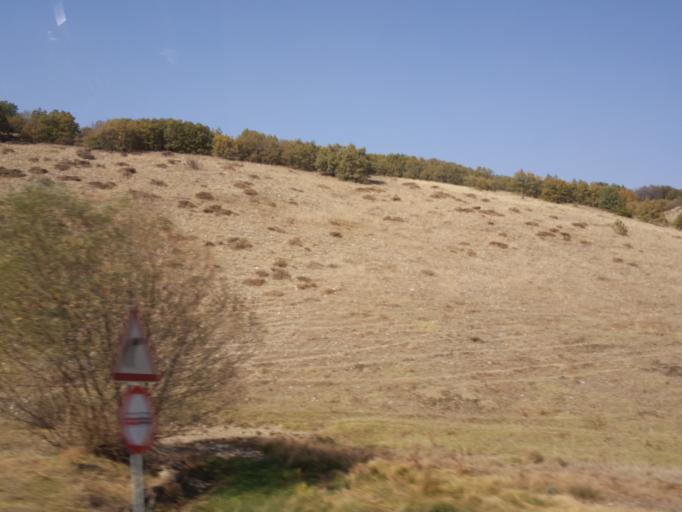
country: TR
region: Corum
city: Bogazkale
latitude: 40.1752
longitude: 34.6723
